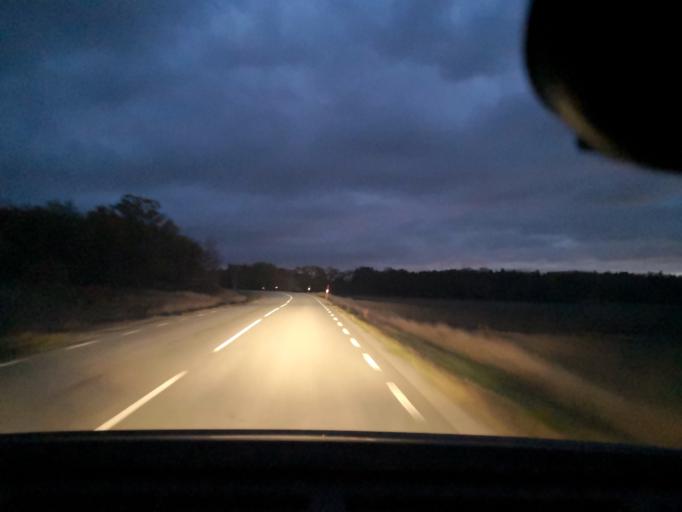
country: SE
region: Uppsala
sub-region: Enkopings Kommun
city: Hummelsta
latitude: 59.5513
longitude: 16.8664
